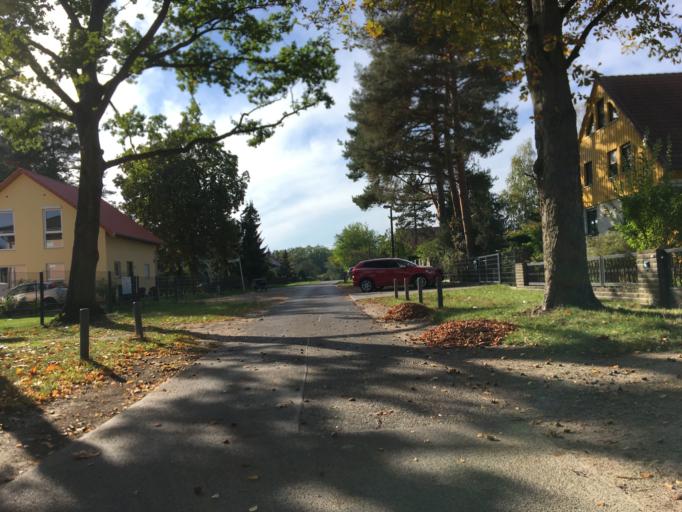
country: DE
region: Berlin
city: Mahlsdorf
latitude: 52.5133
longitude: 13.6297
